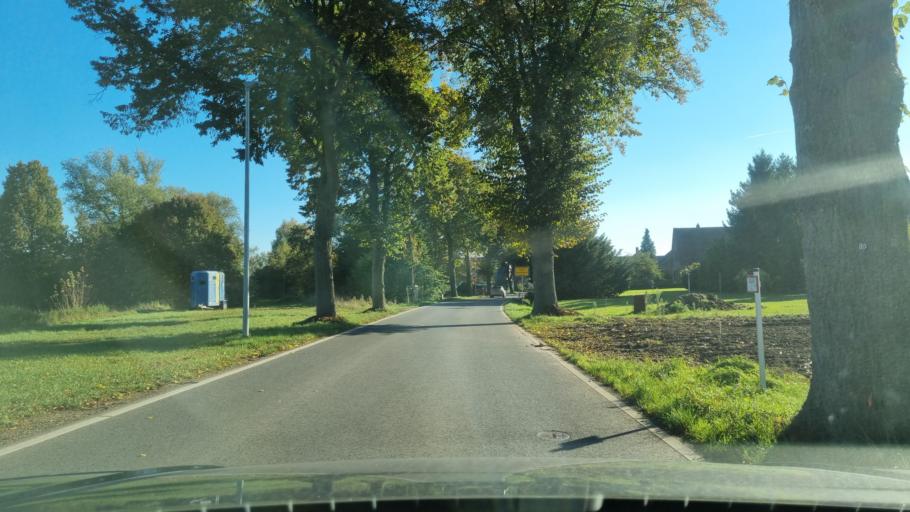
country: DE
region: North Rhine-Westphalia
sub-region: Regierungsbezirk Dusseldorf
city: Kranenburg
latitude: 51.7780
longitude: 6.0208
